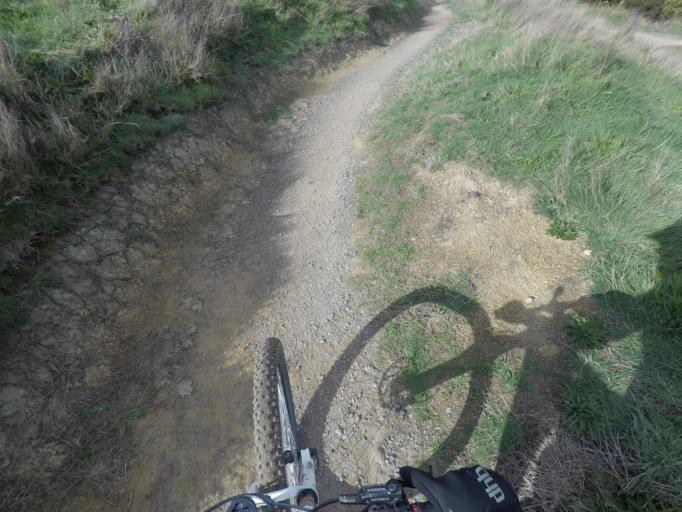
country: NZ
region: Auckland
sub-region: Auckland
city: Manukau City
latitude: -36.9961
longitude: 174.9111
